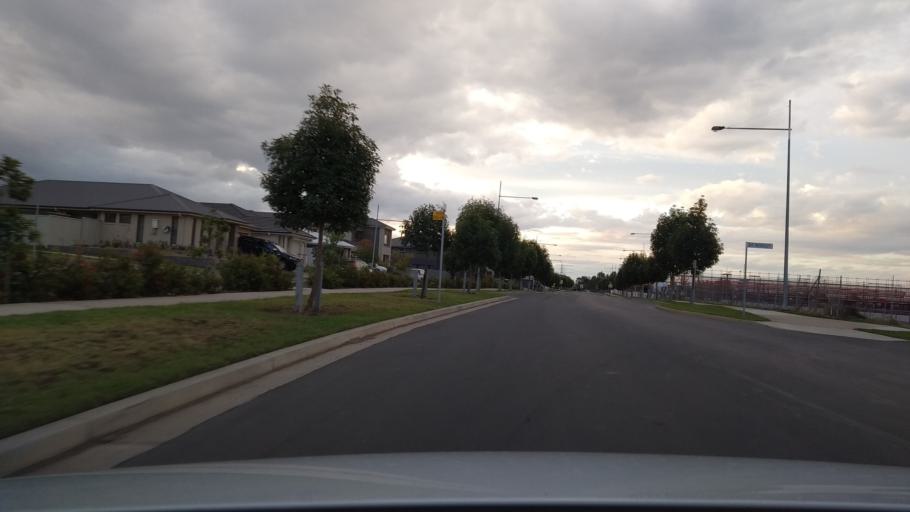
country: AU
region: New South Wales
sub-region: Camden
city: Narellan
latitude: -34.0007
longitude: 150.7346
